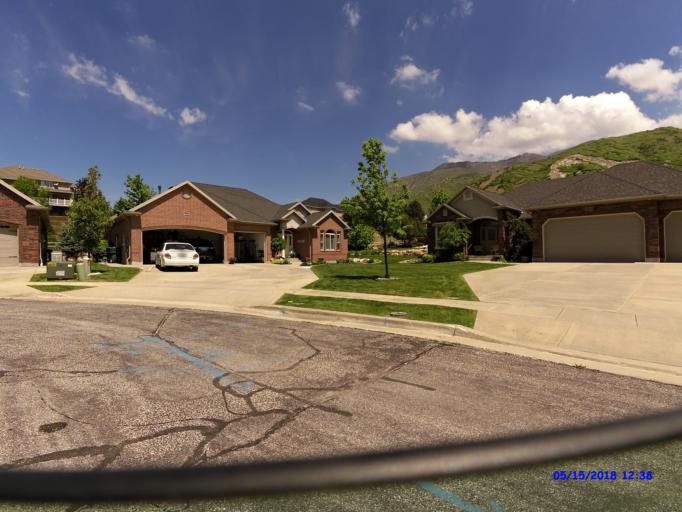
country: US
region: Utah
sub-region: Weber County
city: Uintah
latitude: 41.1633
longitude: -111.9275
